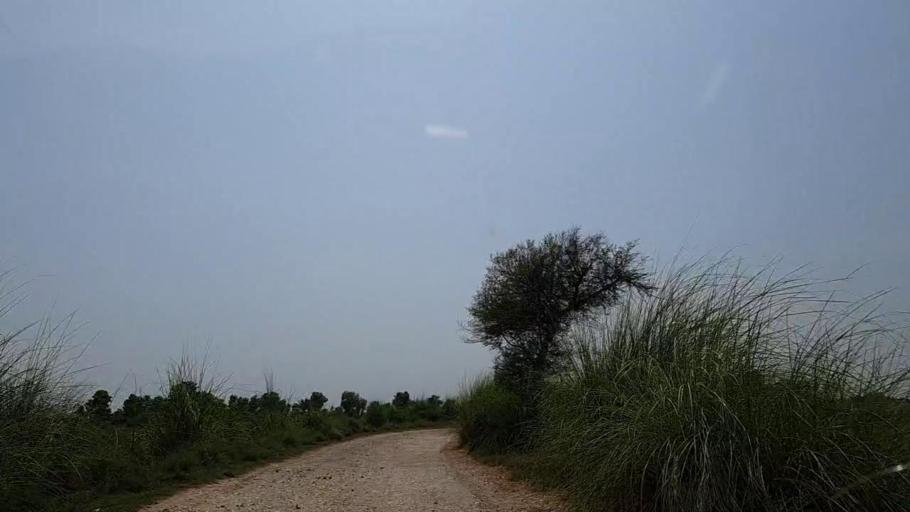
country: PK
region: Sindh
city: Adilpur
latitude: 27.9018
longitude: 69.3601
